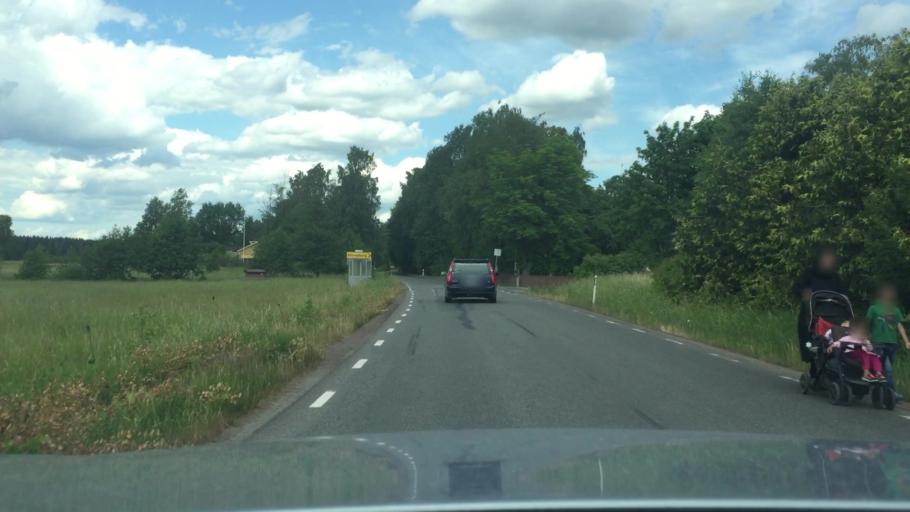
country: SE
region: Vaestra Goetaland
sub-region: Tidaholms Kommun
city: Tidaholm
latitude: 58.1941
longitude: 13.9776
